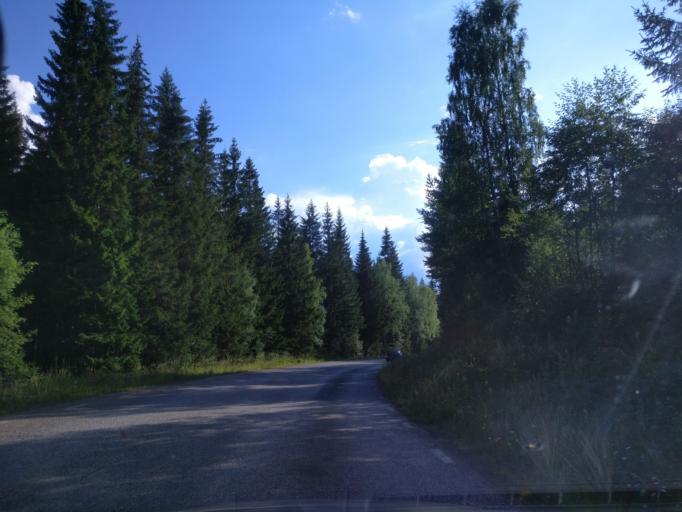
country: SE
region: Dalarna
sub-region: Ludvika Kommun
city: Ludvika
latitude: 60.2720
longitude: 15.0715
